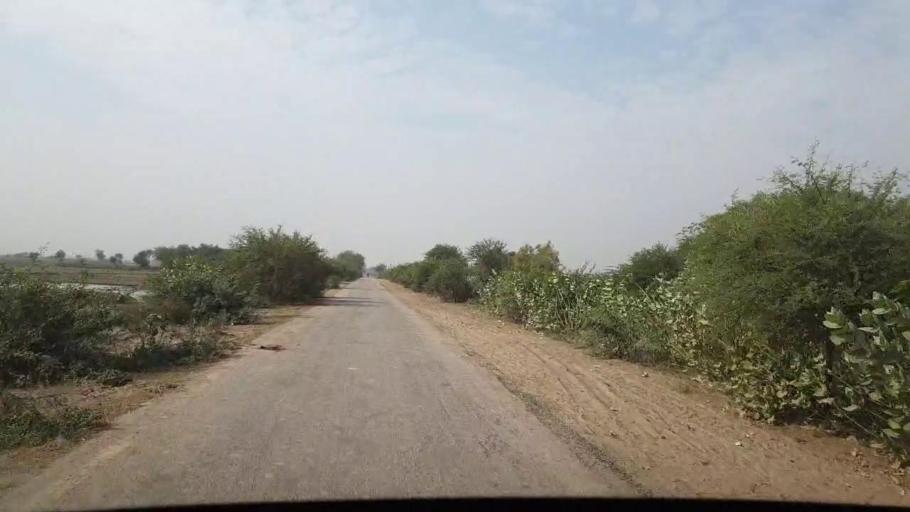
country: PK
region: Sindh
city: Chuhar Jamali
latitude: 24.3873
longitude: 67.9441
